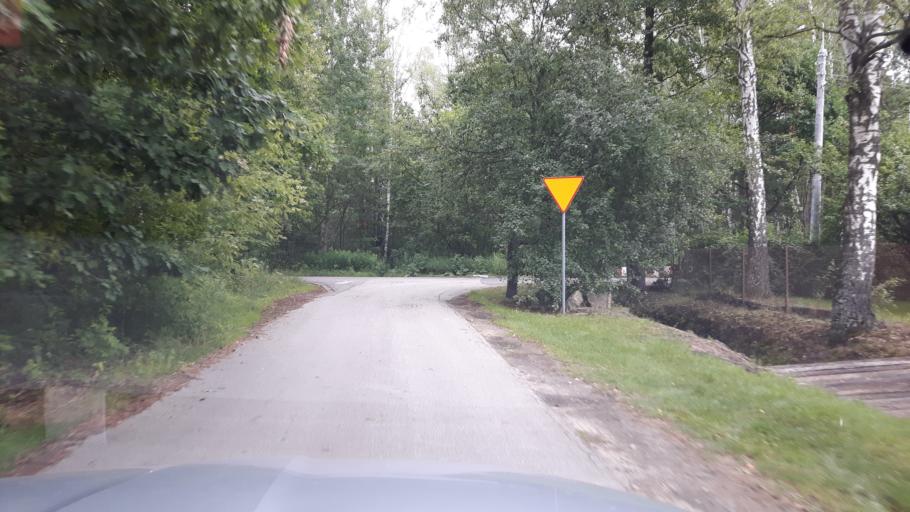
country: PL
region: Masovian Voivodeship
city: Zielonka
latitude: 52.2901
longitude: 21.1649
